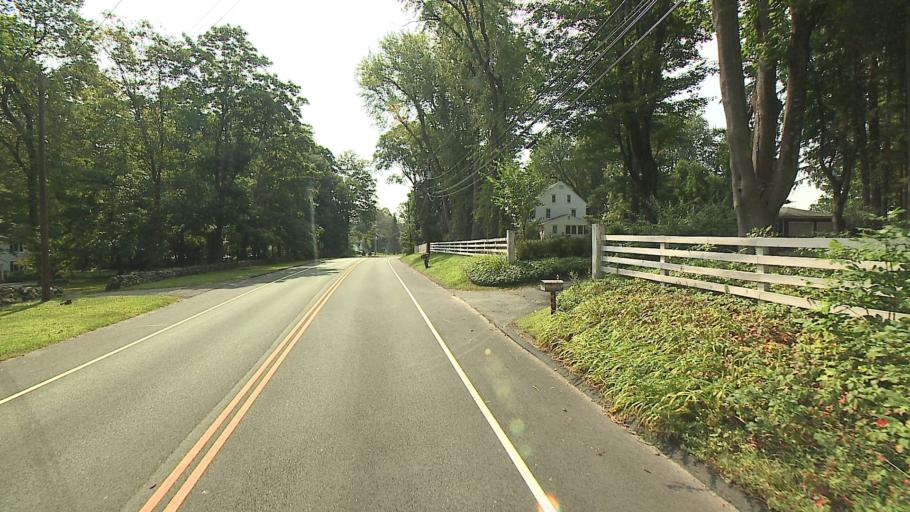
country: US
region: Connecticut
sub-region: Fairfield County
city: Bethel
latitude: 41.3072
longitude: -73.3825
